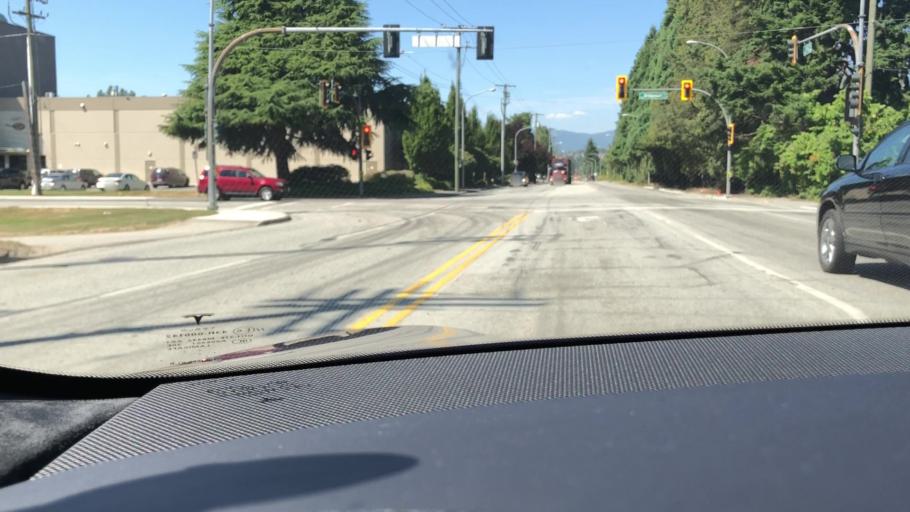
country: CA
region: British Columbia
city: Richmond
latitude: 49.1917
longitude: -123.0692
